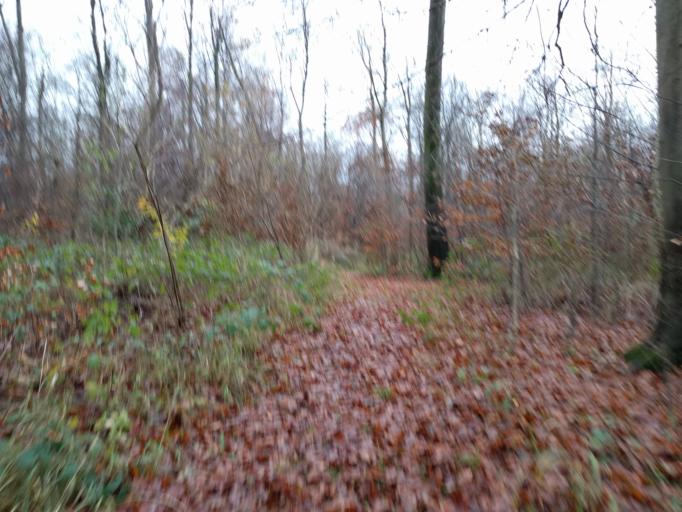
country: DK
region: South Denmark
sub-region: Kerteminde Kommune
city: Langeskov
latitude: 55.3991
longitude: 10.5712
